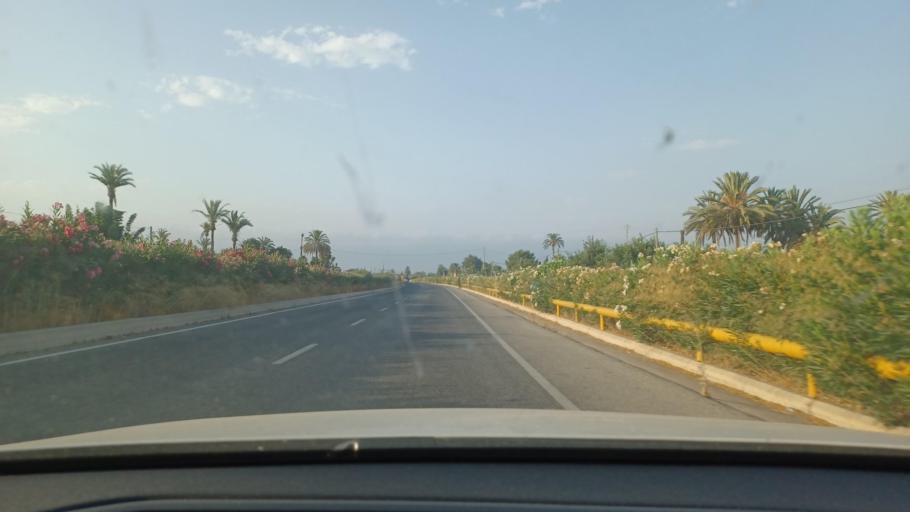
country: ES
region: Valencia
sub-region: Provincia de Alicante
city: Elche
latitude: 38.2120
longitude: -0.6976
